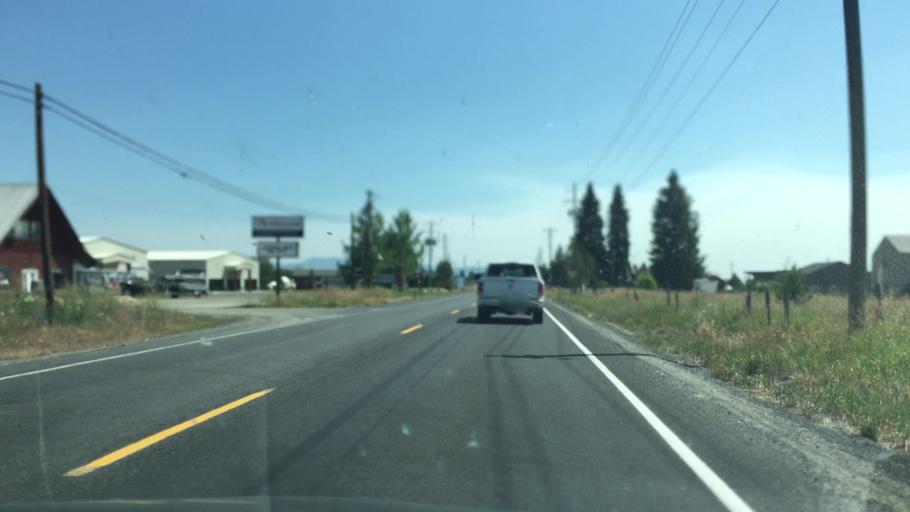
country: US
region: Idaho
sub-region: Valley County
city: McCall
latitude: 44.8376
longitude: -116.0862
